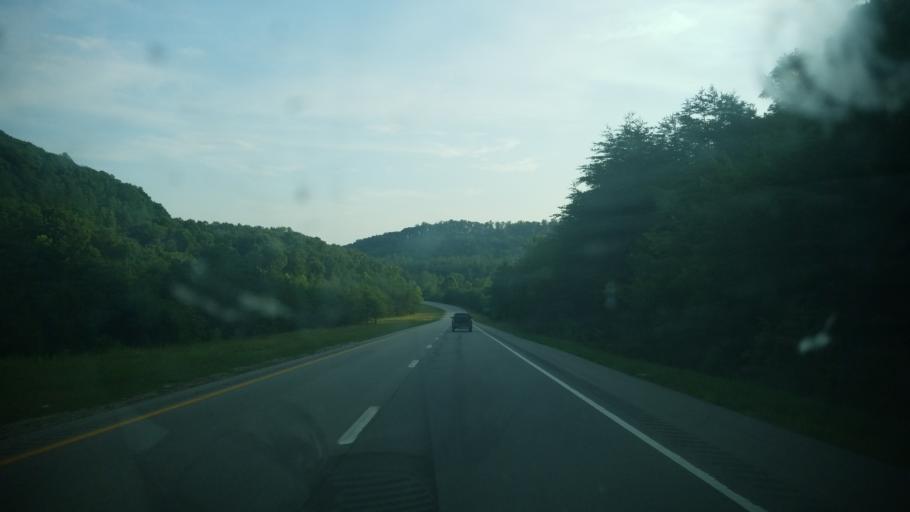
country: US
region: Ohio
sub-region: Adams County
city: Peebles
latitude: 39.0176
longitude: -83.2917
